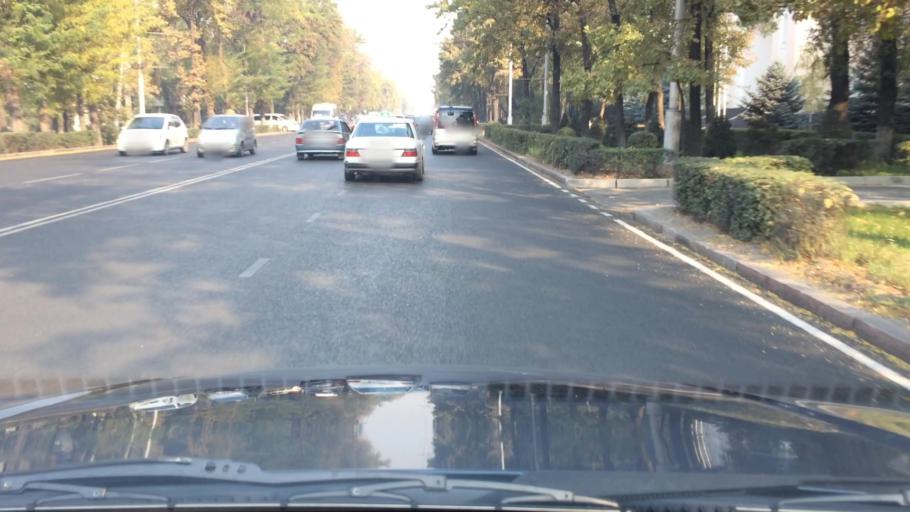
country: KG
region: Chuy
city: Bishkek
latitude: 42.8515
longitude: 74.5865
